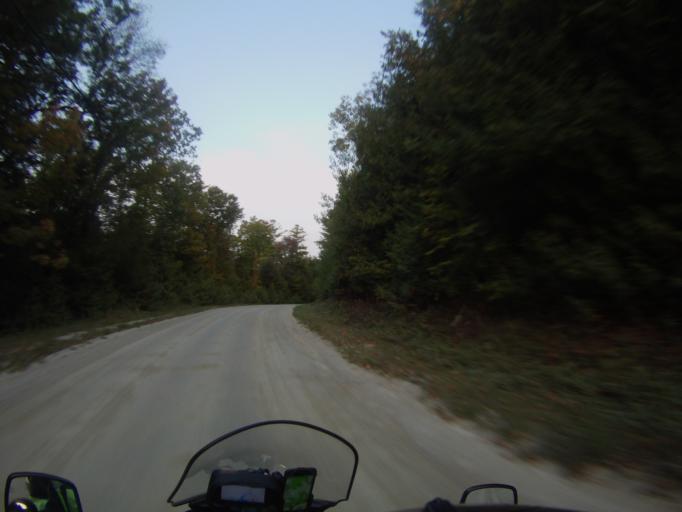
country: US
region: Vermont
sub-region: Rutland County
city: Brandon
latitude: 43.7832
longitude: -73.1303
